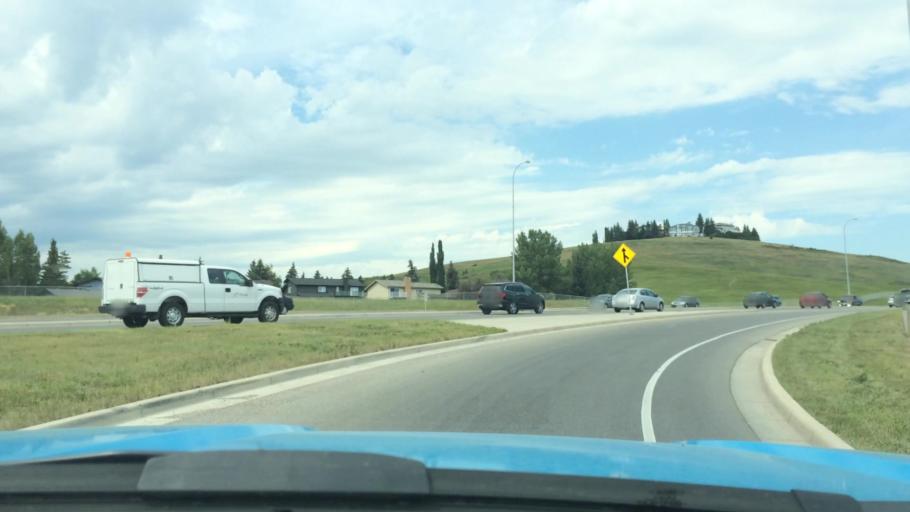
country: CA
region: Alberta
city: Calgary
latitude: 51.1093
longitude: -114.1395
